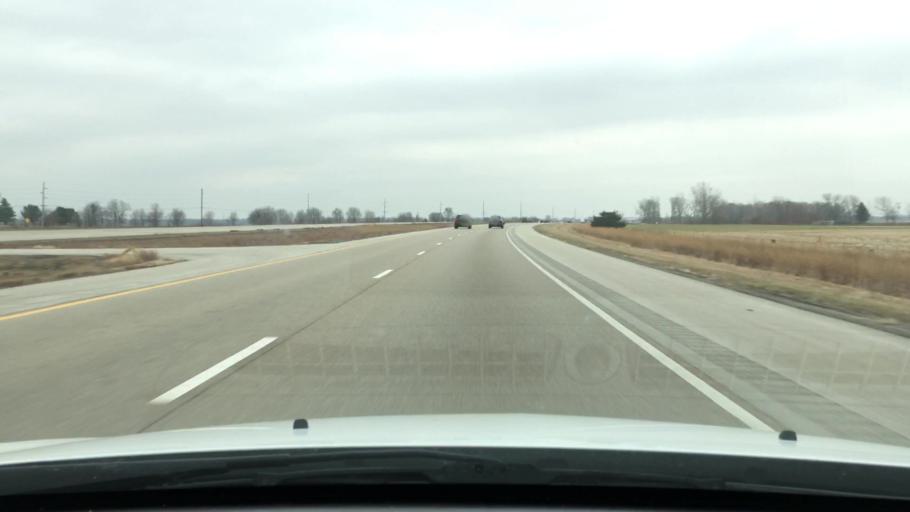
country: US
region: Illinois
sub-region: Logan County
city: Lincoln
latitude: 40.1953
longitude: -89.3048
